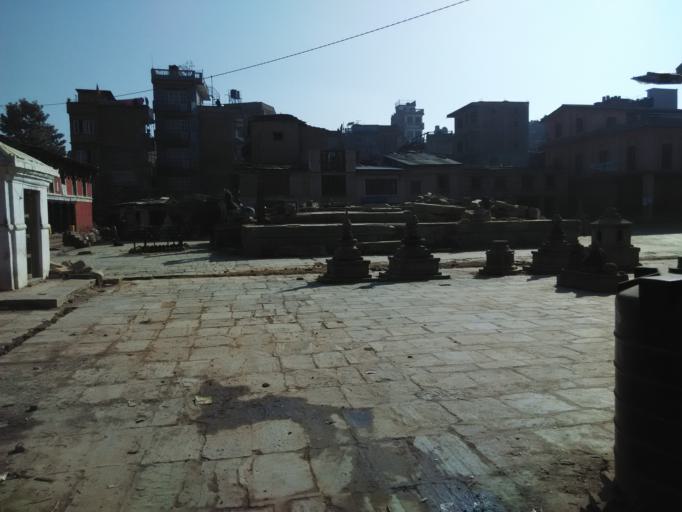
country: NP
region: Central Region
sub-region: Bagmati Zone
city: Patan
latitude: 27.6299
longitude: 85.3018
